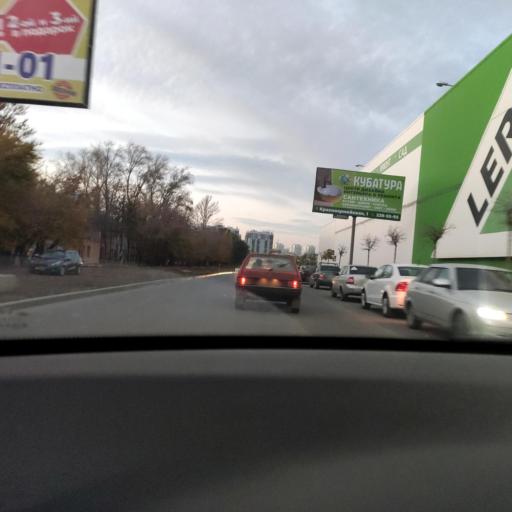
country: RU
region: Samara
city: Samara
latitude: 53.2072
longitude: 50.1940
